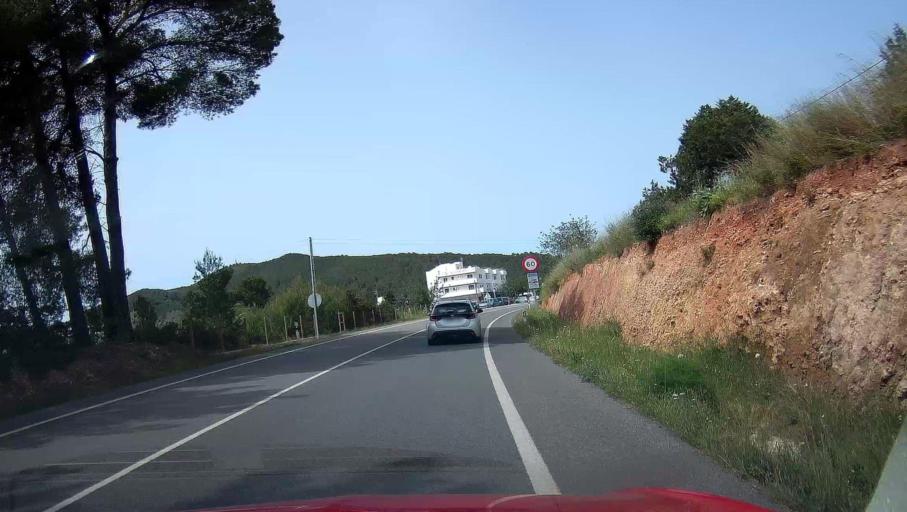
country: ES
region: Balearic Islands
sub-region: Illes Balears
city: Sant Joan de Labritja
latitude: 39.0655
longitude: 1.4944
